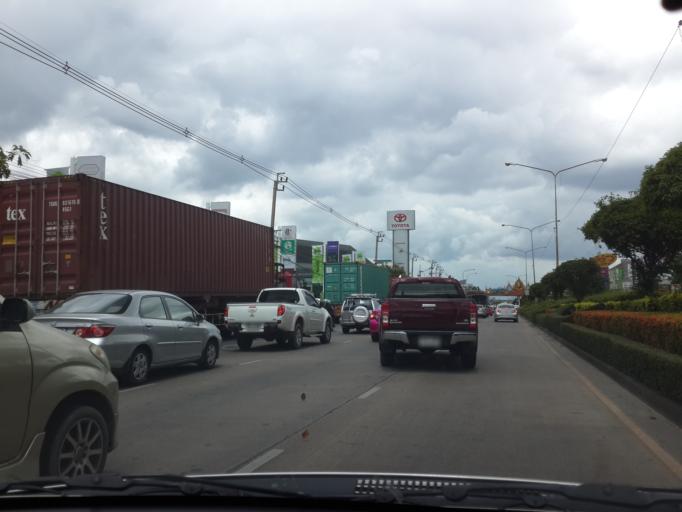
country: TH
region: Bangkok
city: Bueng Kum
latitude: 13.7734
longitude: 100.6670
